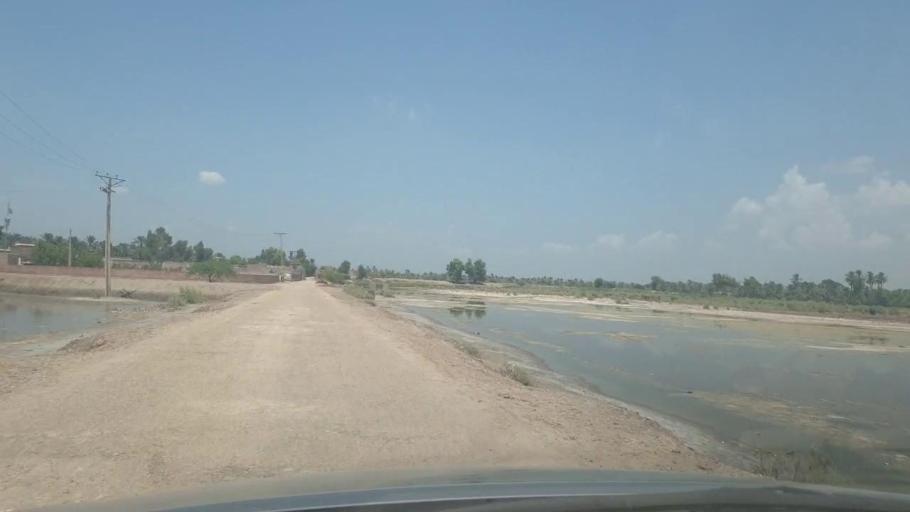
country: PK
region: Sindh
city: Kot Diji
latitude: 27.4188
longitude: 68.7364
